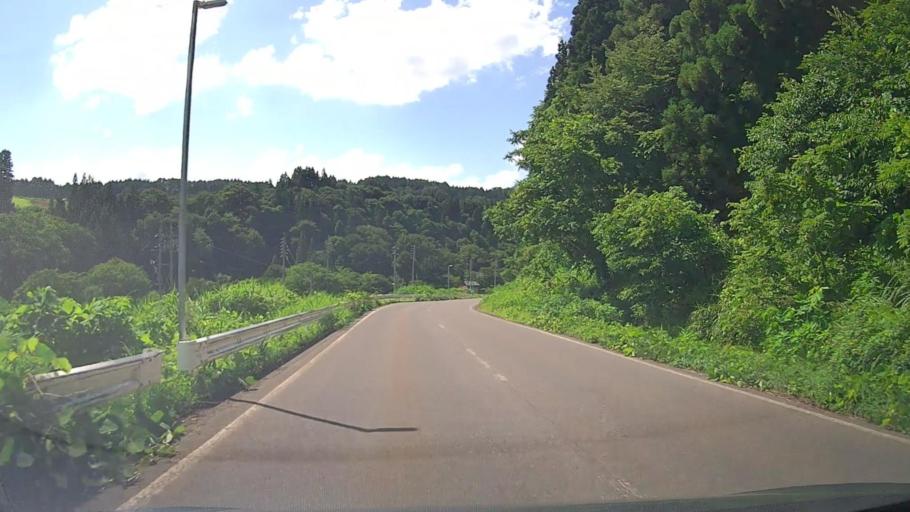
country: JP
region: Nagano
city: Iiyama
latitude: 36.9247
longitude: 138.4273
